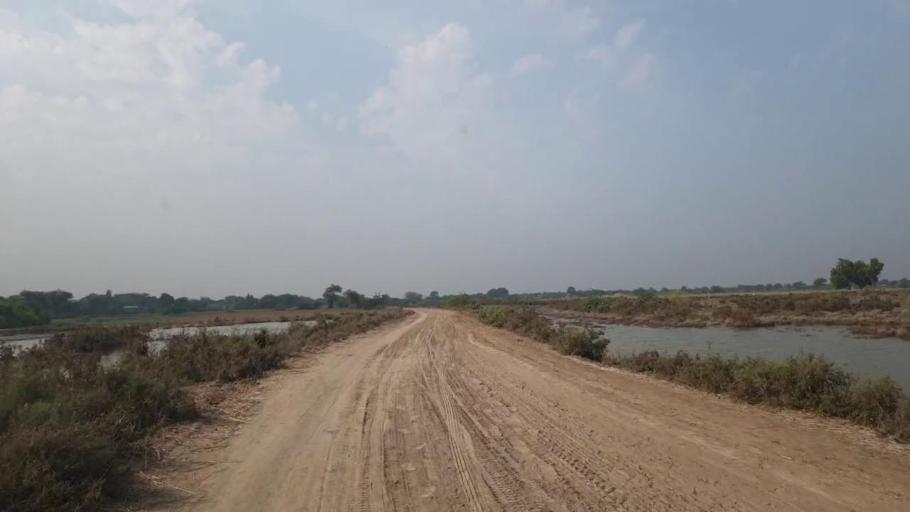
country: PK
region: Sindh
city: Talhar
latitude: 24.8425
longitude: 68.8076
